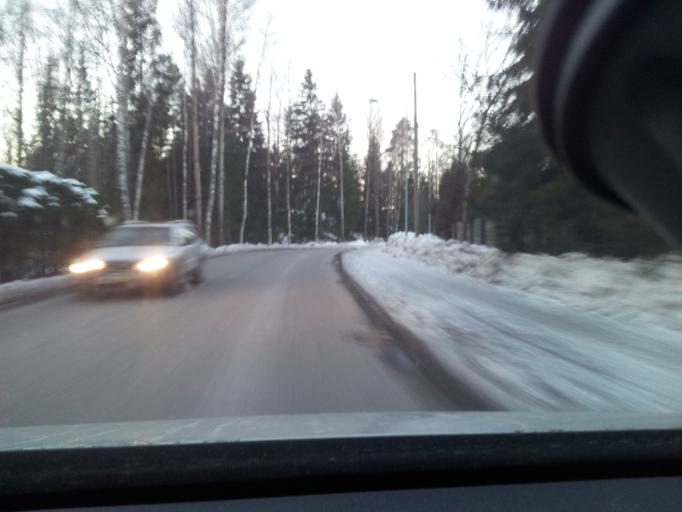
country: FI
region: Uusimaa
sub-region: Helsinki
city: Koukkuniemi
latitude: 60.1641
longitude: 24.7199
